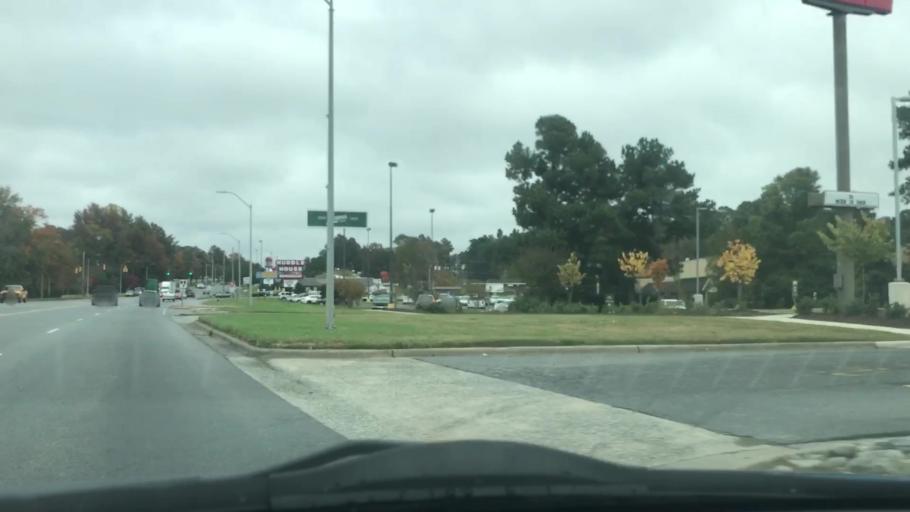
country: US
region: North Carolina
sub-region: Randolph County
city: Asheboro
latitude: 35.6869
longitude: -79.8266
